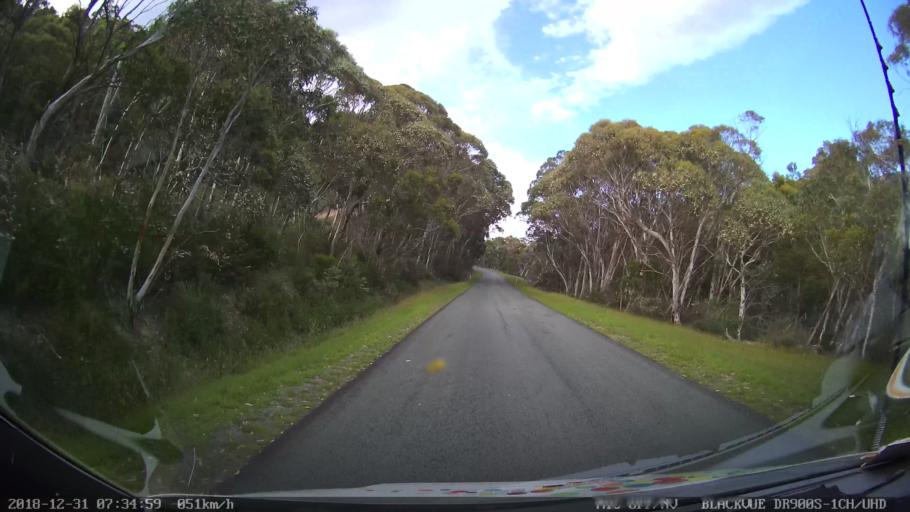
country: AU
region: New South Wales
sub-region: Snowy River
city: Jindabyne
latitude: -36.3324
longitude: 148.4476
